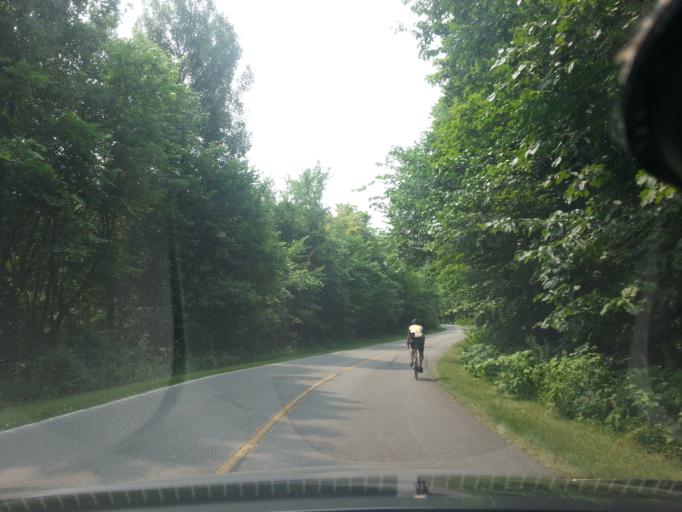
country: CA
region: Quebec
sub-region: Outaouais
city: Wakefield
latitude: 45.5191
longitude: -75.8559
